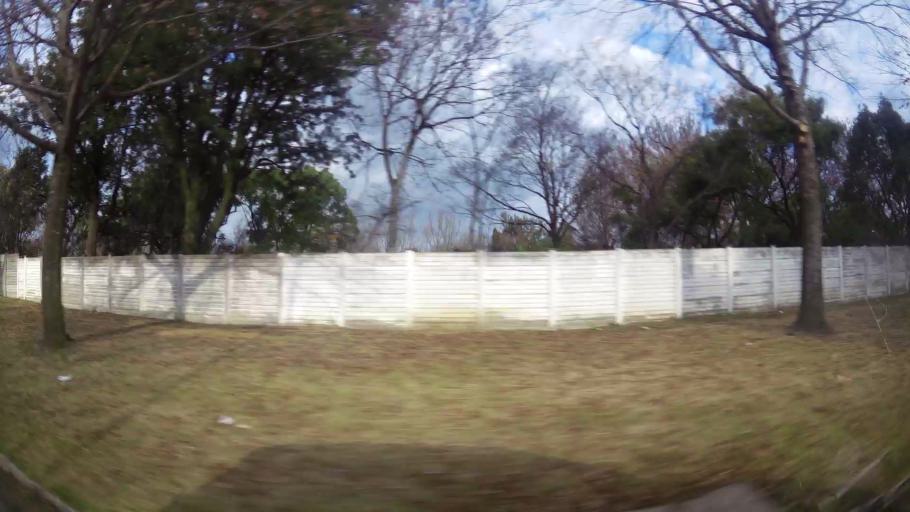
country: ZA
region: Orange Free State
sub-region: Fezile Dabi District Municipality
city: Sasolburg
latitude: -26.7983
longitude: 27.8210
